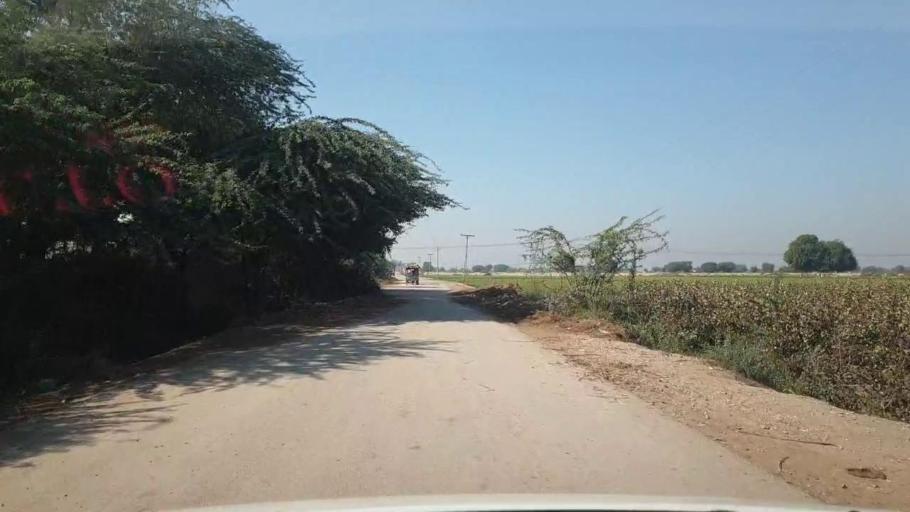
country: PK
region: Sindh
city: Bhan
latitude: 26.6456
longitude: 67.7290
